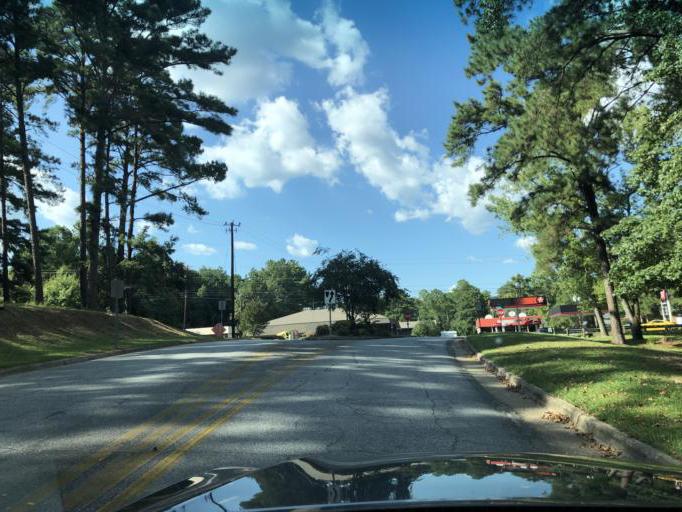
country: US
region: Georgia
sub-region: Muscogee County
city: Columbus
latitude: 32.5390
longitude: -84.9340
